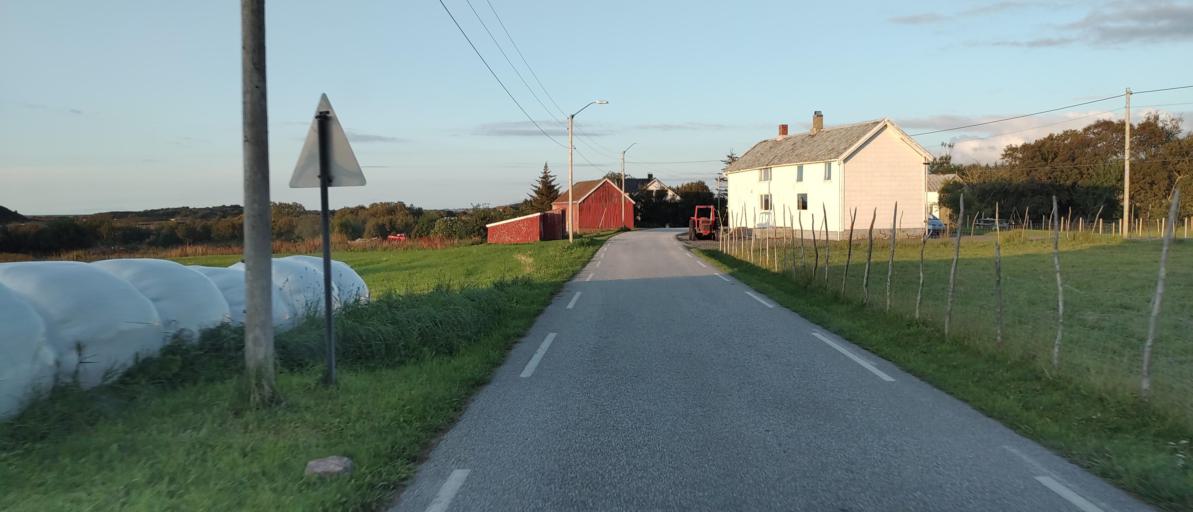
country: NO
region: More og Romsdal
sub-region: Fraena
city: Elnesvagen
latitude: 62.9980
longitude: 7.2262
